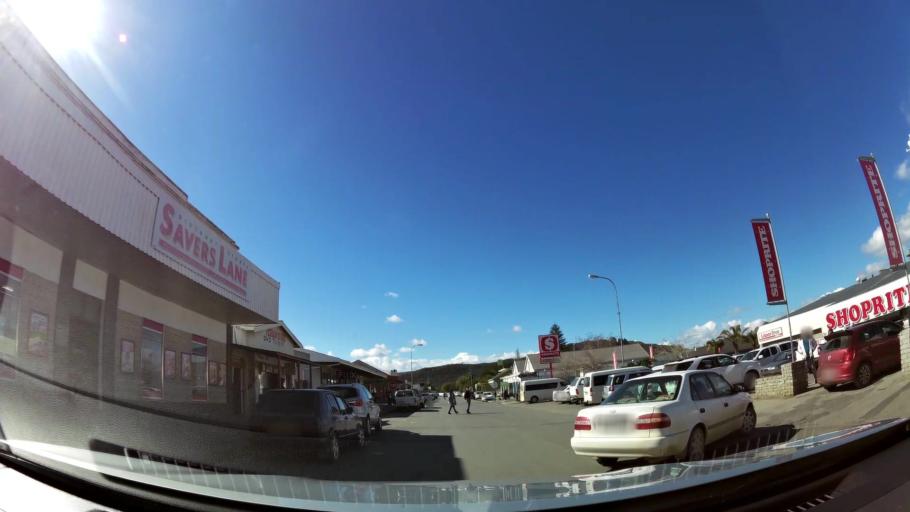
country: ZA
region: Western Cape
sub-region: Cape Winelands District Municipality
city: Ashton
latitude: -33.7861
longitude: 20.1249
